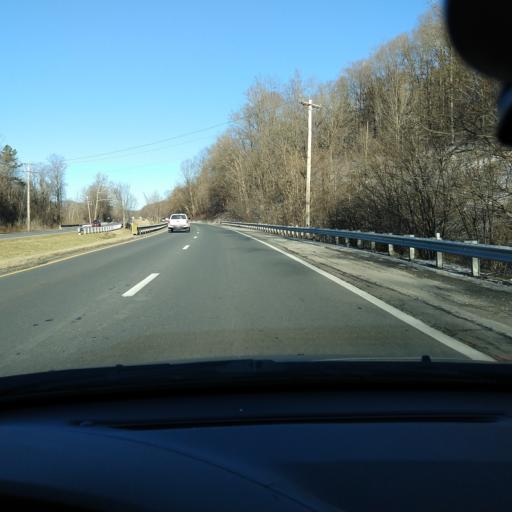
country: US
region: Virginia
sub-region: Botetourt County
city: Laymantown
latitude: 37.3391
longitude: -79.8527
